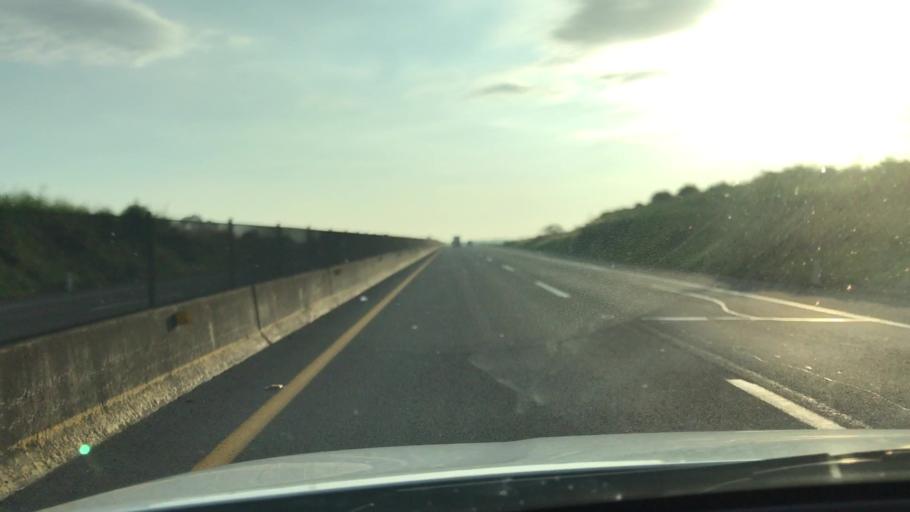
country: MX
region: Jalisco
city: Tepatitlan de Morelos
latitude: 20.8574
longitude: -102.7679
